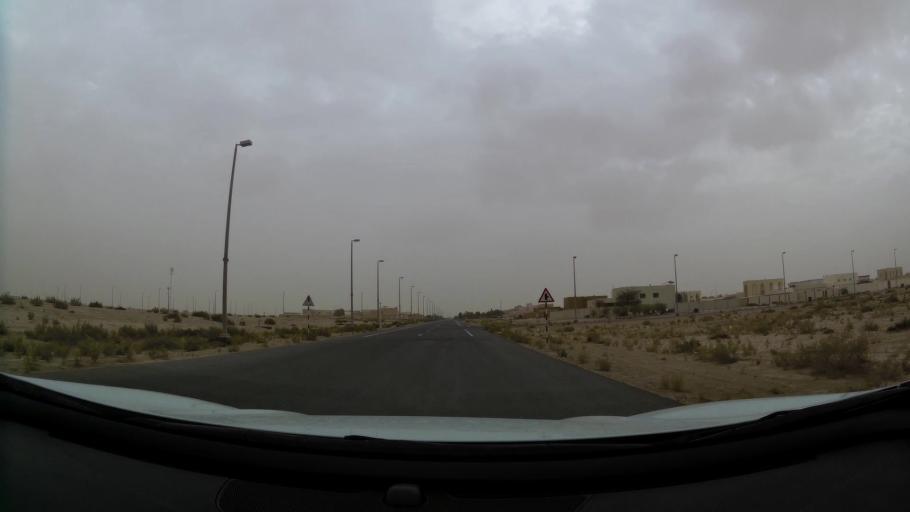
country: AE
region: Abu Dhabi
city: Abu Dhabi
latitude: 24.4183
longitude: 54.6988
